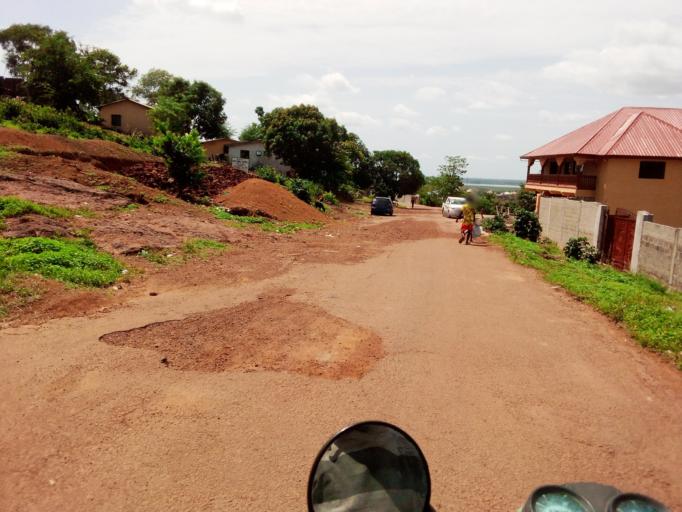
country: SL
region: Western Area
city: Waterloo
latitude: 8.3503
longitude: -13.0790
